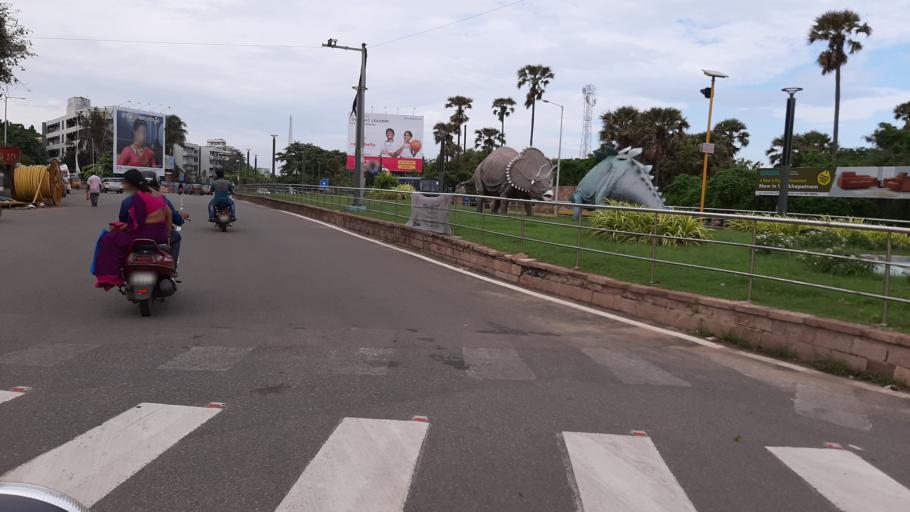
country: IN
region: Andhra Pradesh
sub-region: Vishakhapatnam
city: Yarada
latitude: 17.7220
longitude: 83.3357
